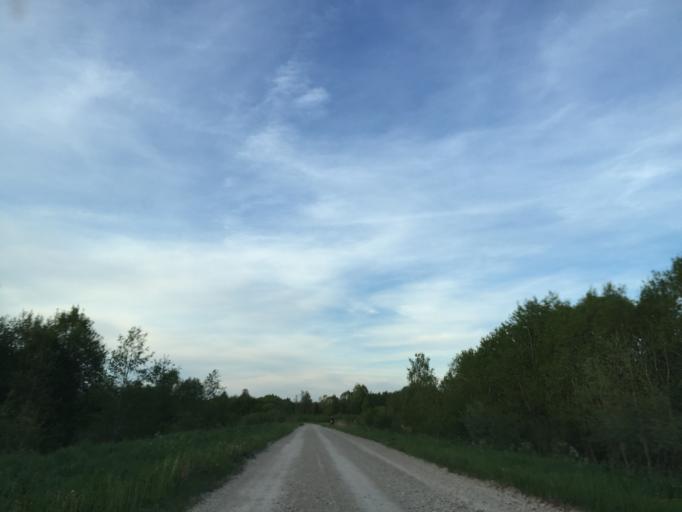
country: LV
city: Tireli
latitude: 56.7508
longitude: 23.5339
